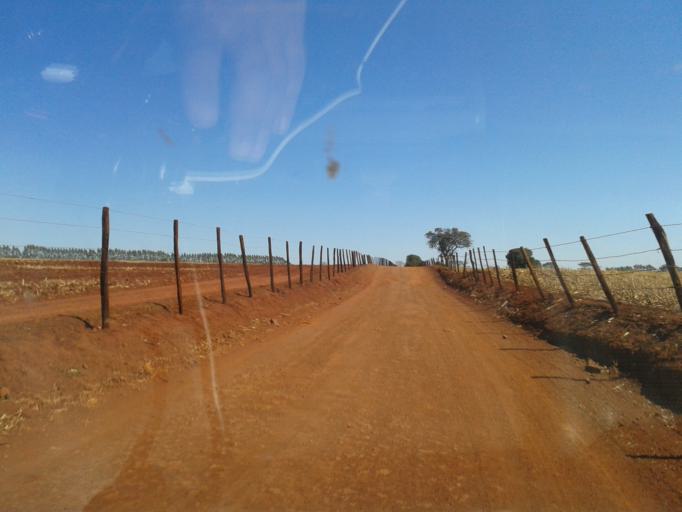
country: BR
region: Minas Gerais
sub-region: Centralina
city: Centralina
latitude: -18.5861
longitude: -49.1853
